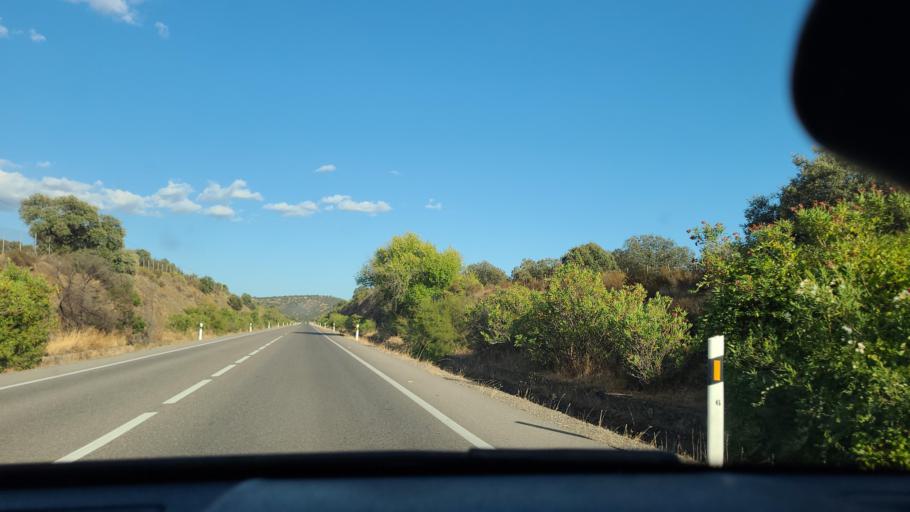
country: ES
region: Andalusia
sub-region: Province of Cordoba
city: Belmez
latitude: 38.2056
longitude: -5.1219
